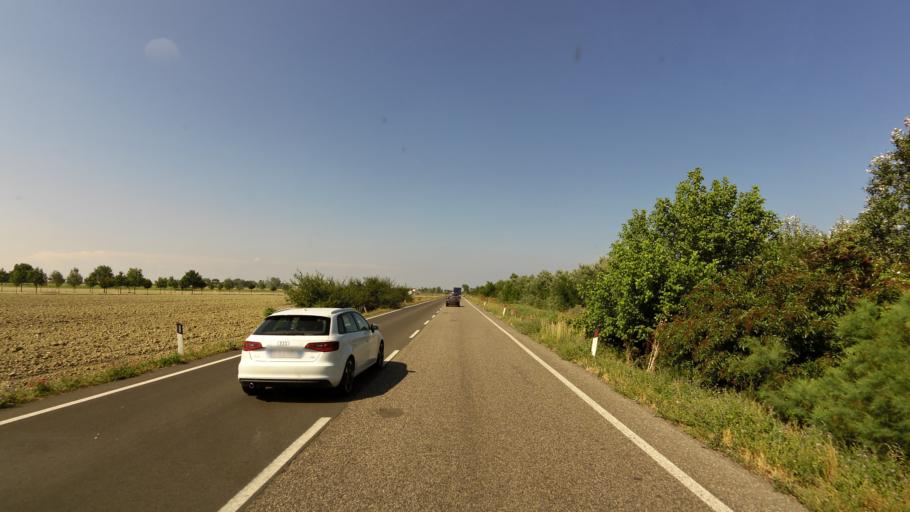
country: IT
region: Emilia-Romagna
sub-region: Provincia di Ravenna
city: Marina Romea
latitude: 44.5530
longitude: 12.2432
